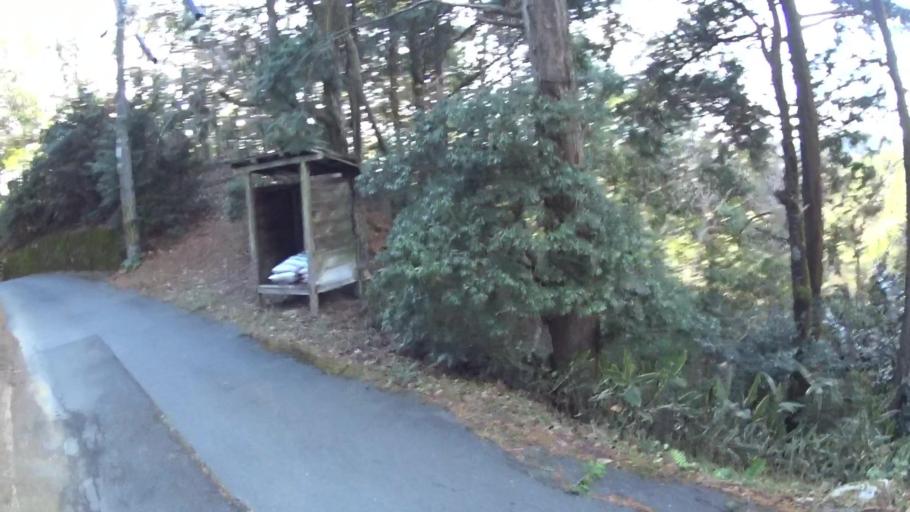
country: JP
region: Kyoto
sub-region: Kyoto-shi
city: Kamigyo-ku
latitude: 35.0766
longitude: 135.7184
